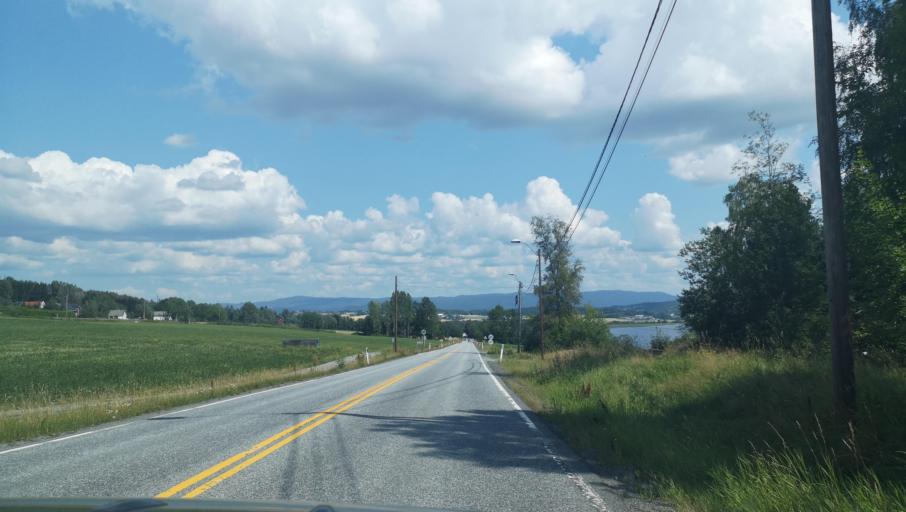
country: NO
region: Buskerud
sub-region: Ovre Eiker
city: Hokksund
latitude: 59.7037
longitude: 9.8064
